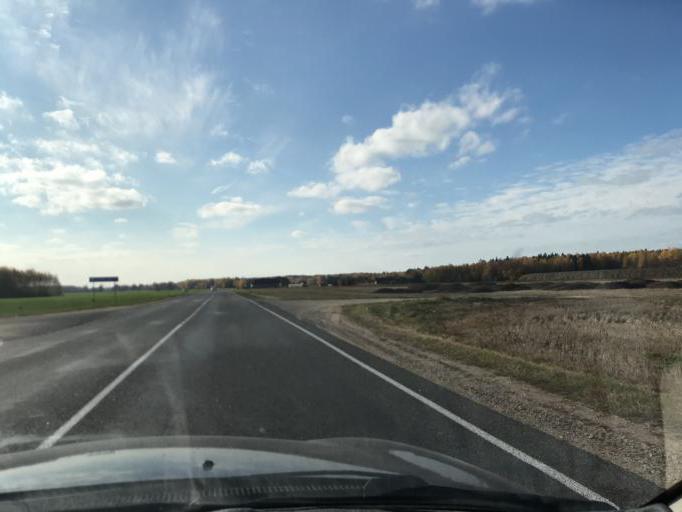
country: BY
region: Grodnenskaya
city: Voranava
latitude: 54.1906
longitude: 25.3437
